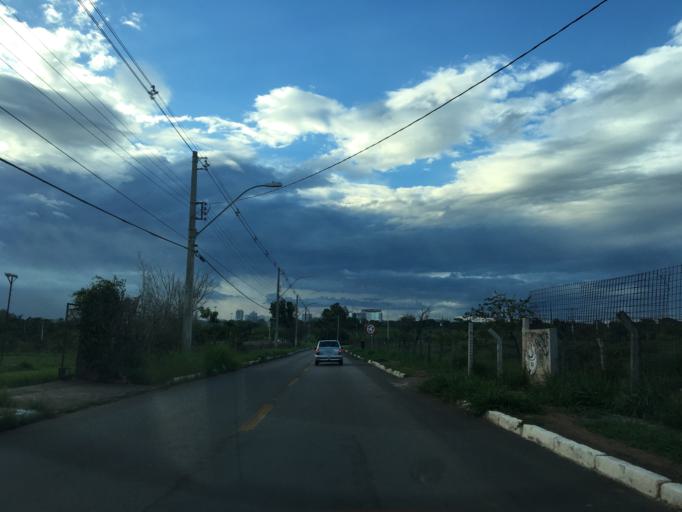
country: BR
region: Federal District
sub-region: Brasilia
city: Brasilia
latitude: -15.8147
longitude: -47.8464
